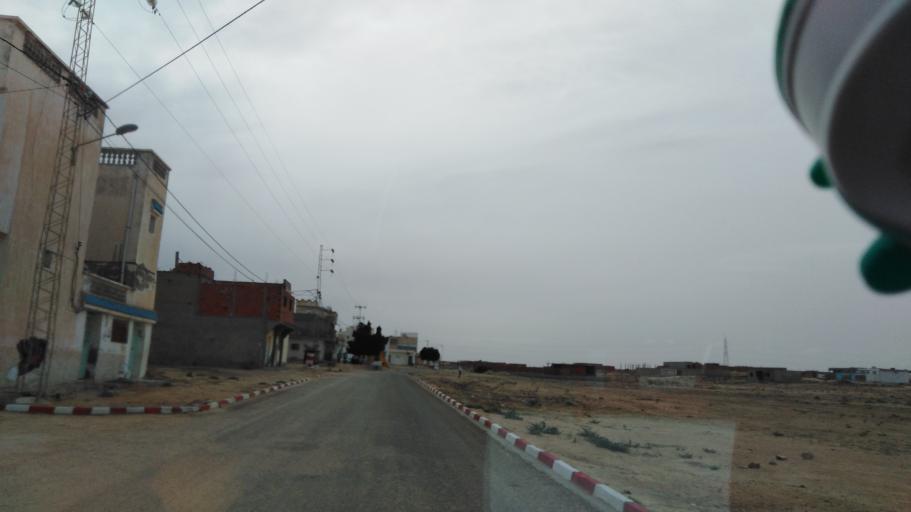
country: TN
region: Qabis
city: Gabes
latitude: 33.9513
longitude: 10.0028
